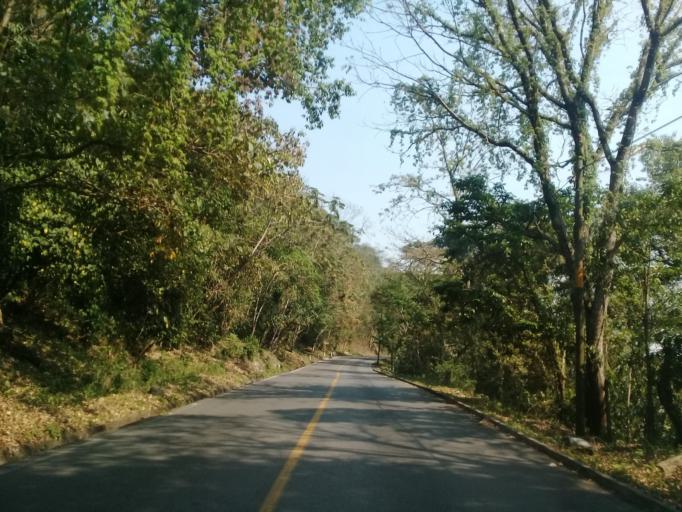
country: MX
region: Veracruz
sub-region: Ixtaczoquitlan
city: Campo Chico
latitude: 18.8443
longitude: -97.0290
